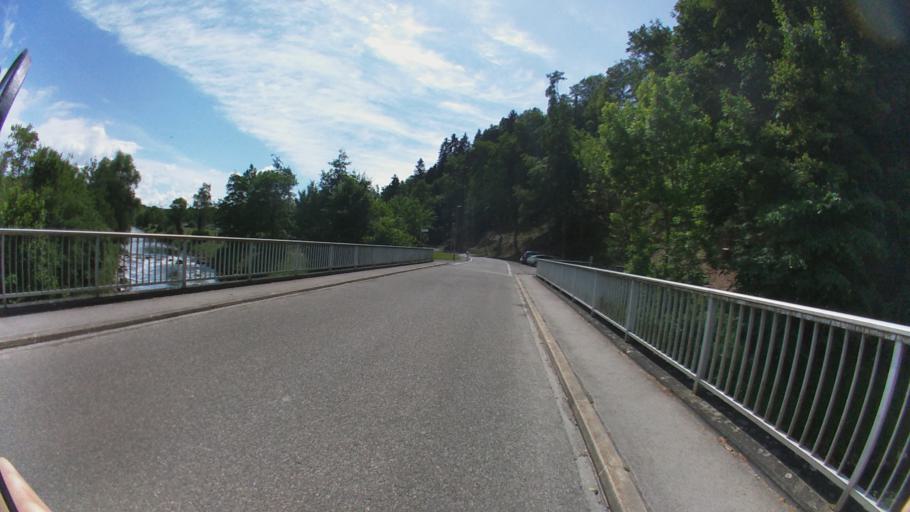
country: CH
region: Zurich
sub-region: Bezirk Buelach
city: Glattfelden
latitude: 47.5511
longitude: 8.5063
